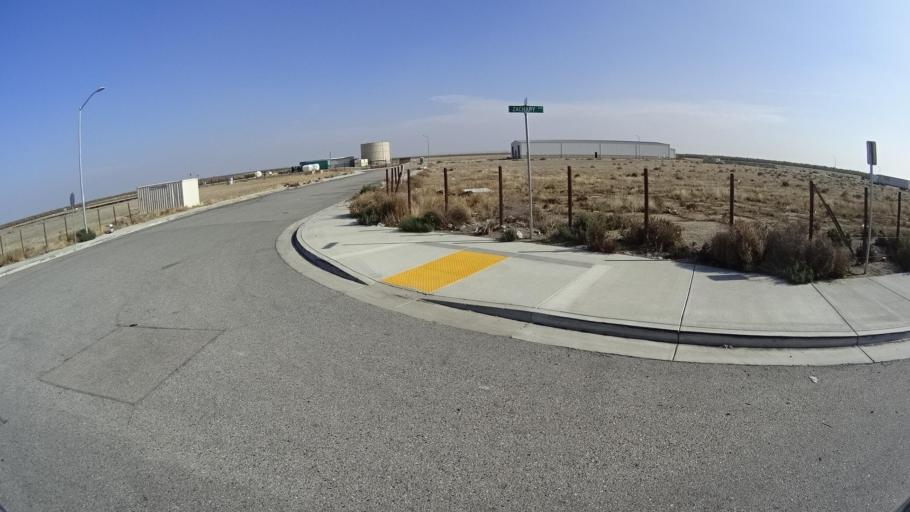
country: US
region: California
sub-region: Kern County
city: Shafter
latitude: 35.5320
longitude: -119.1871
